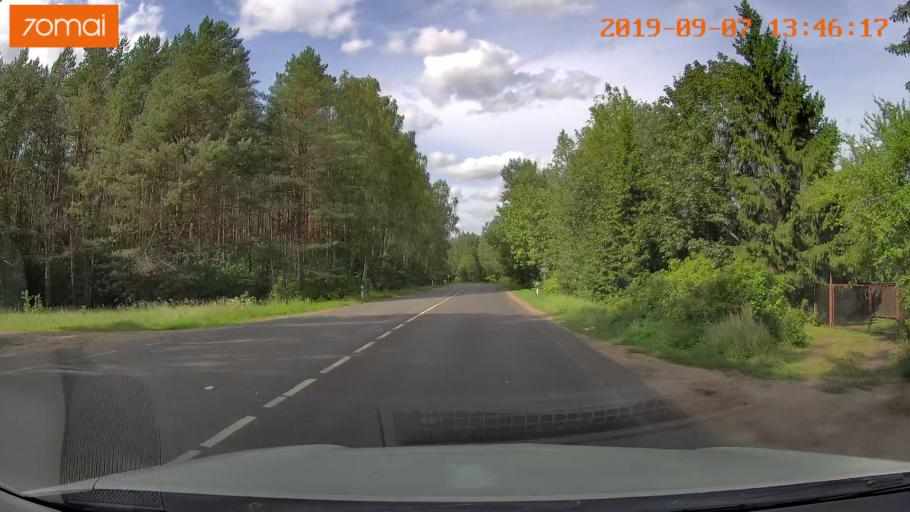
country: LT
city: Baltoji Voke
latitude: 54.5901
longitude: 25.2344
